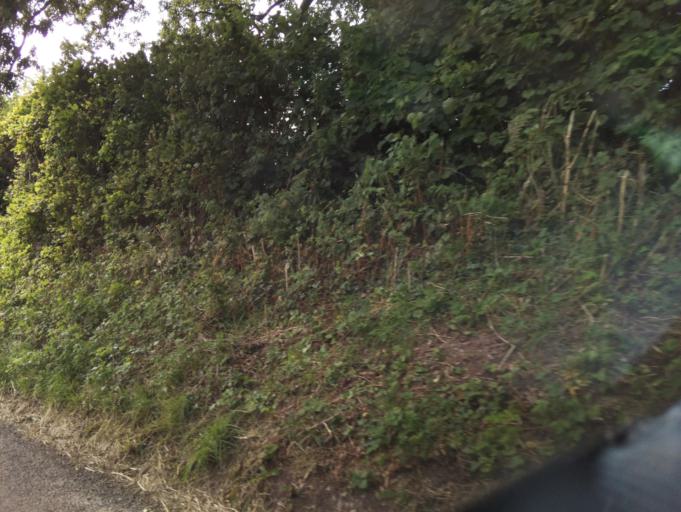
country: GB
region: England
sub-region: Borough of Torbay
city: Paignton
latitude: 50.4022
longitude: -3.6068
